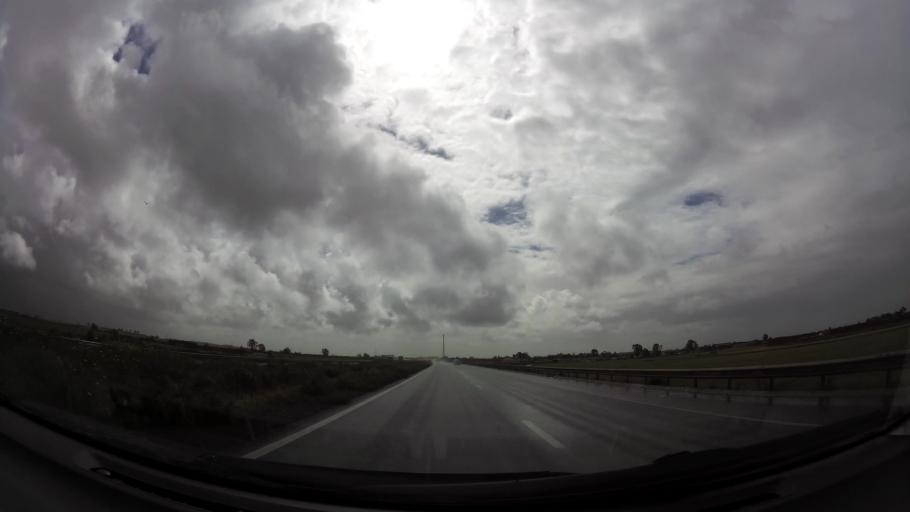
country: MA
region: Grand Casablanca
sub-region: Nouaceur
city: Dar Bouazza
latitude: 33.3902
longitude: -7.8753
